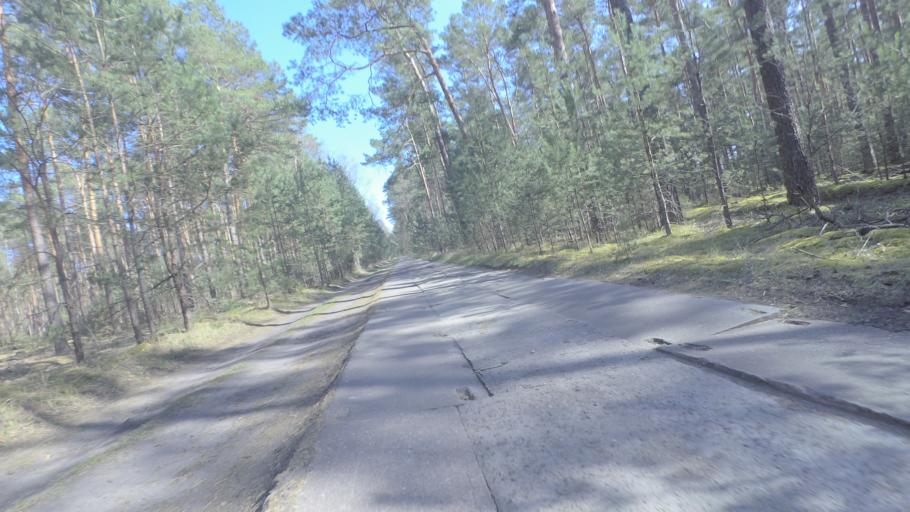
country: DE
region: Brandenburg
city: Halbe
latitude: 52.1730
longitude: 13.7469
